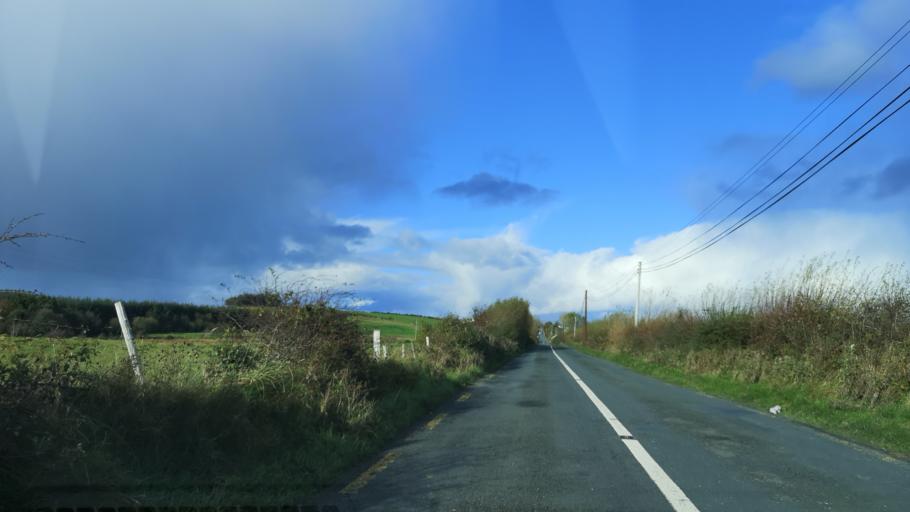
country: IE
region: Connaught
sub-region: Maigh Eo
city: Castlebar
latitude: 53.7638
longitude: -9.3769
